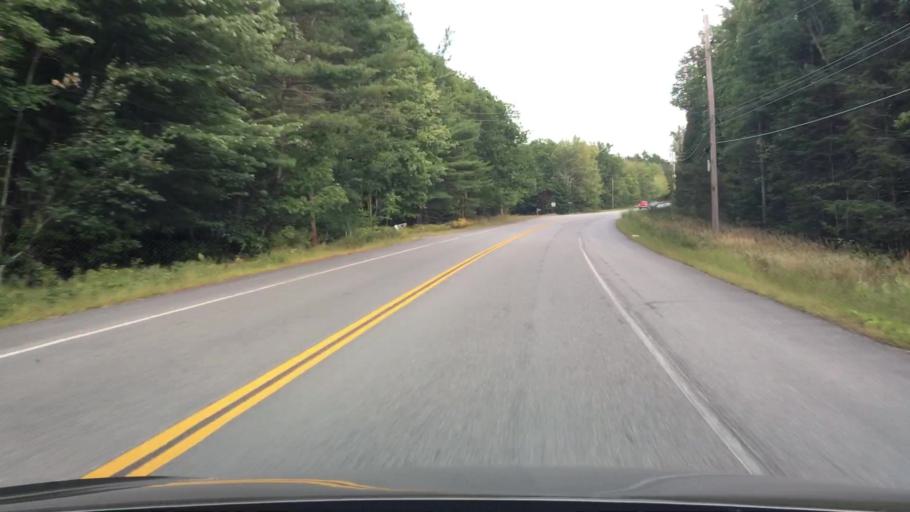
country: US
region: Maine
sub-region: Cumberland County
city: Bridgton
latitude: 44.0661
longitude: -70.7516
